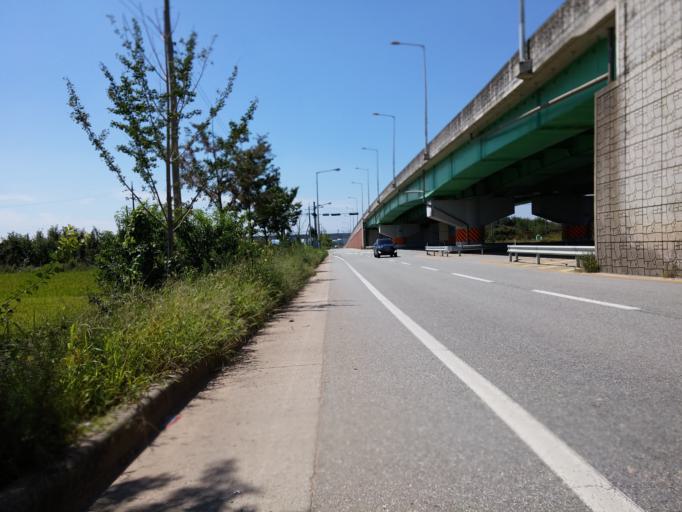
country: KR
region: Chungcheongbuk-do
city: Cheongju-si
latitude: 36.6197
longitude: 127.3425
